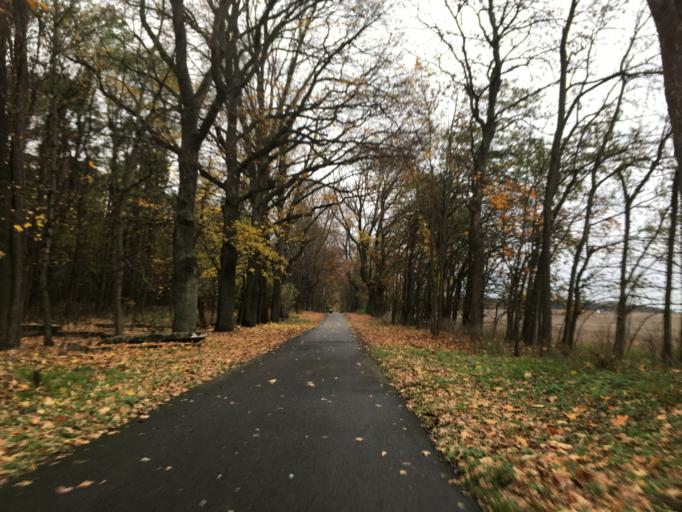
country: DE
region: Brandenburg
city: Gross Lindow
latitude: 52.2932
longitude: 14.5213
